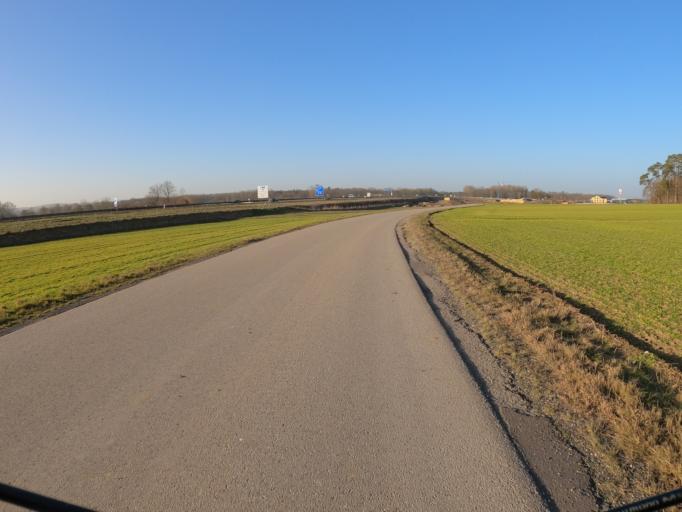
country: DE
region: Bavaria
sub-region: Swabia
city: Holzheim
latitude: 48.4094
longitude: 10.0948
